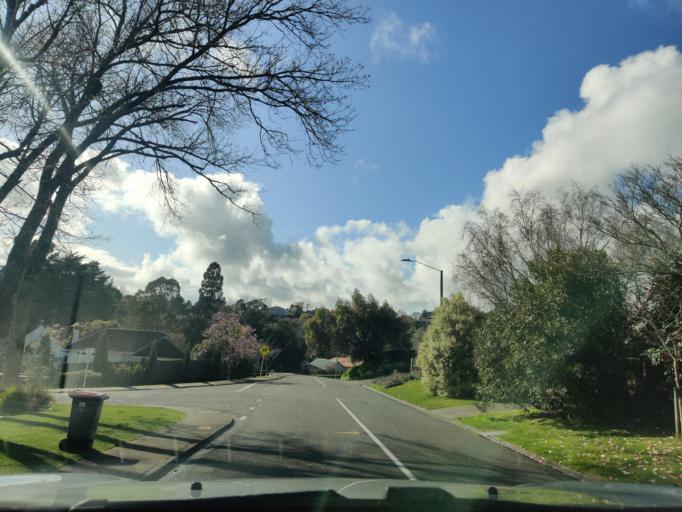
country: NZ
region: Hawke's Bay
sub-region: Hastings District
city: Hastings
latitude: -39.6743
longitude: 176.8911
